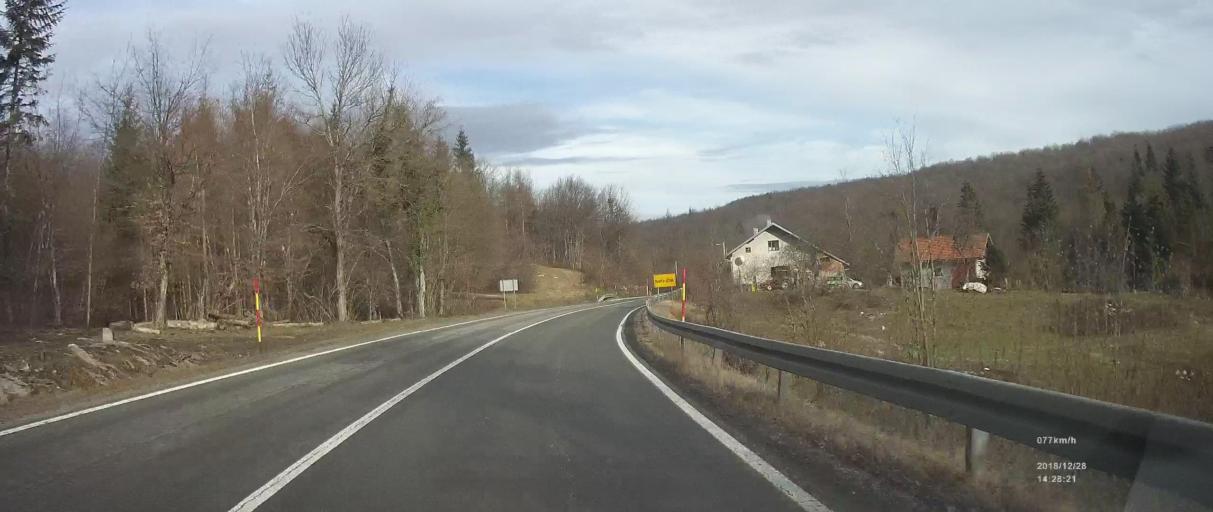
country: HR
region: Primorsko-Goranska
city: Vrbovsko
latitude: 45.4095
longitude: 15.1131
